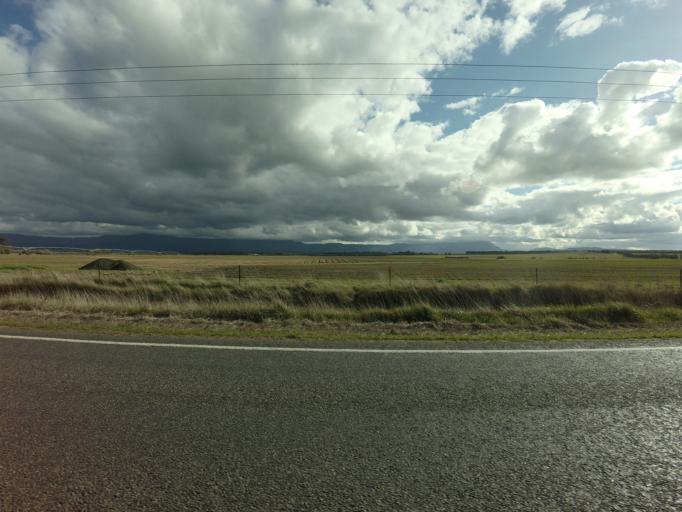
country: AU
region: Tasmania
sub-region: Northern Midlands
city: Longford
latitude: -41.7081
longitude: 147.0799
